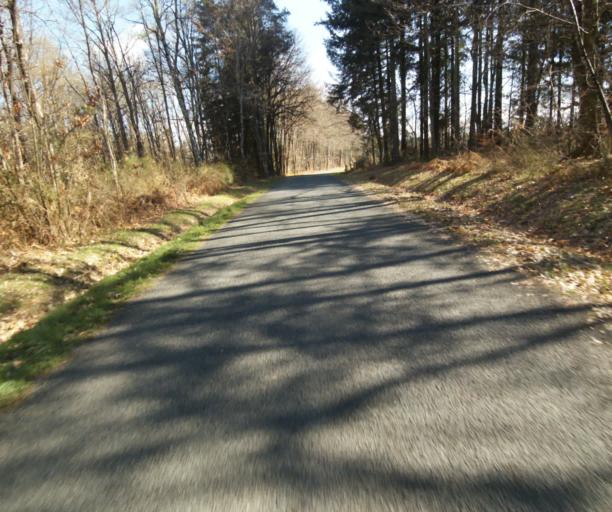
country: FR
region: Limousin
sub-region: Departement de la Correze
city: Correze
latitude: 45.2470
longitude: 1.9209
